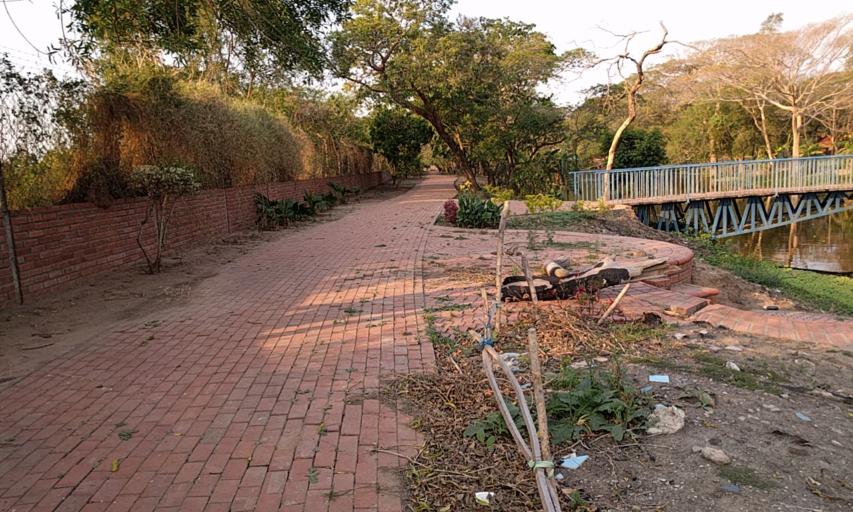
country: BO
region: Santa Cruz
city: Warnes
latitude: -17.4484
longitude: -63.1865
